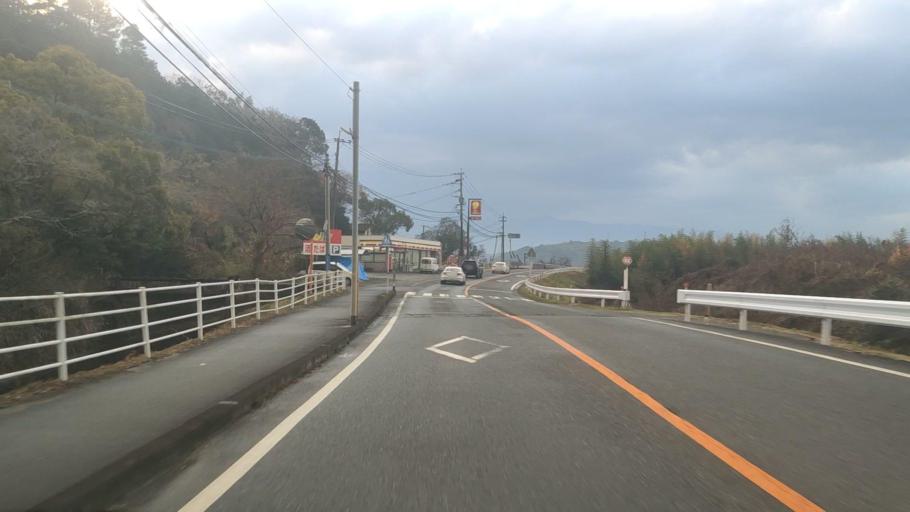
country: JP
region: Kumamoto
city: Uto
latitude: 32.6971
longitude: 130.7876
